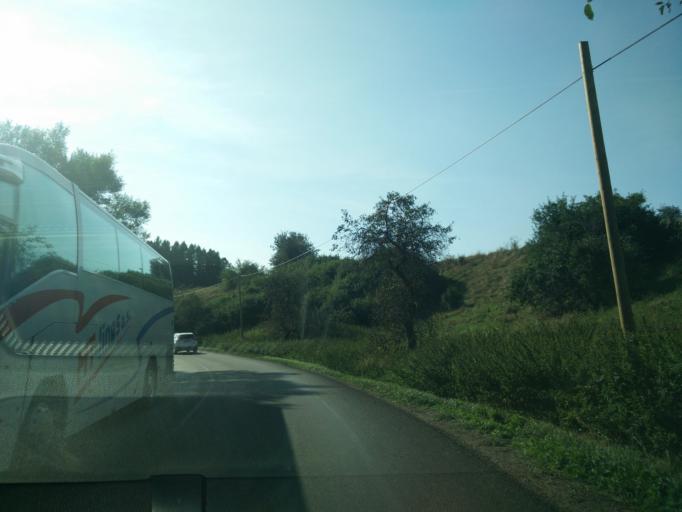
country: SK
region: Zilinsky
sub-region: Okres Martin
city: Martin
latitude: 48.9479
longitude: 18.8390
